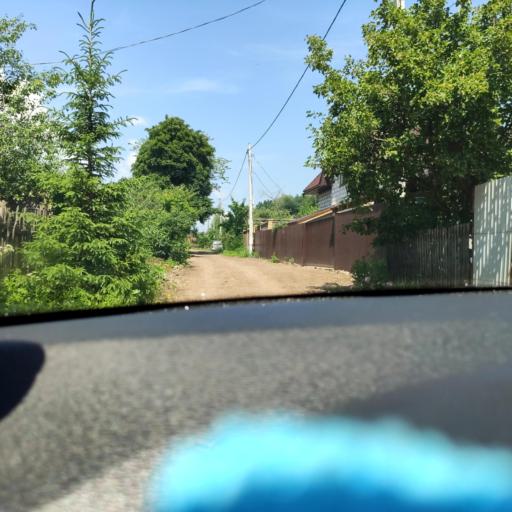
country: RU
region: Samara
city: Petra-Dubrava
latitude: 53.2648
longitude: 50.2655
